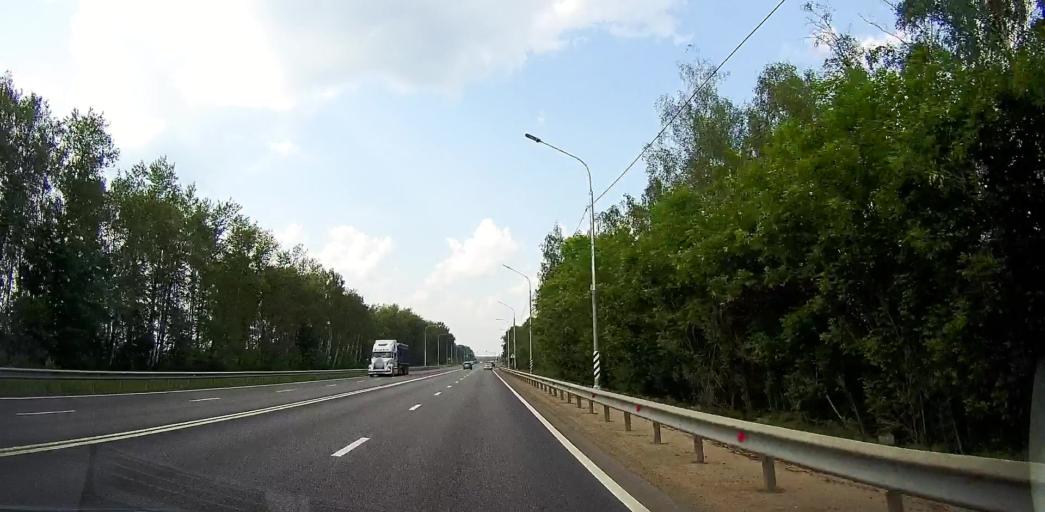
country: RU
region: Moskovskaya
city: Mikhnevo
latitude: 55.1015
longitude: 37.9476
